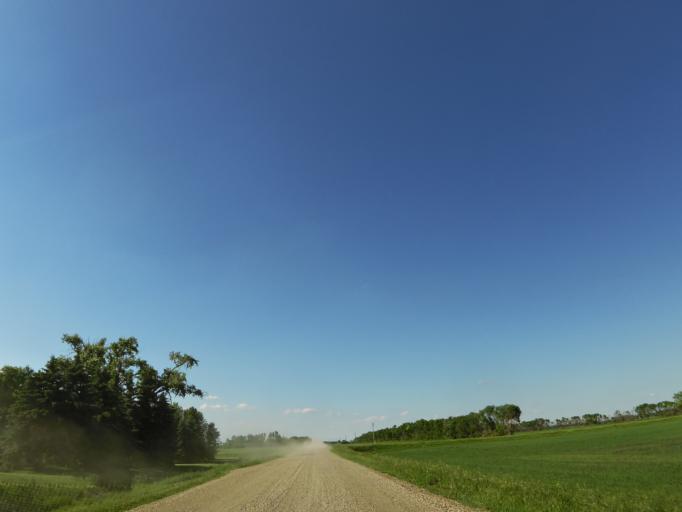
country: US
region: North Dakota
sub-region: Walsh County
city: Grafton
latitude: 48.3532
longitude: -97.2564
